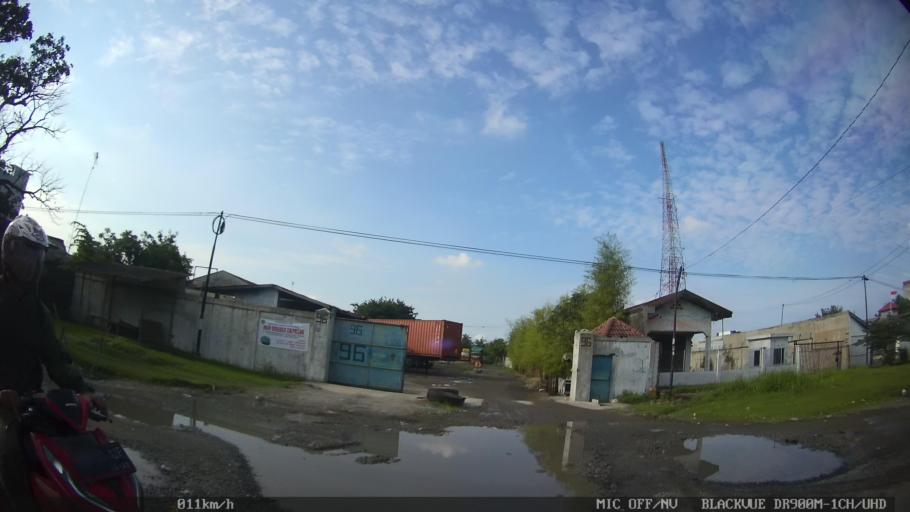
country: ID
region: North Sumatra
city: Medan
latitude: 3.6157
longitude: 98.6465
